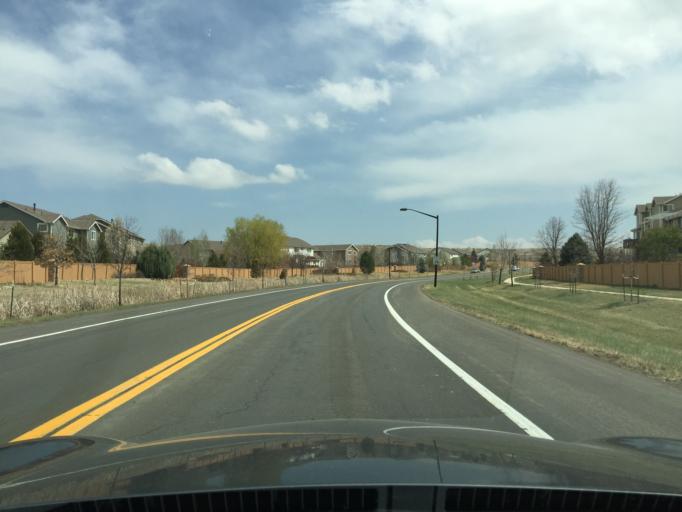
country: US
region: Colorado
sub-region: Boulder County
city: Erie
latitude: 40.0209
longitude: -105.0411
